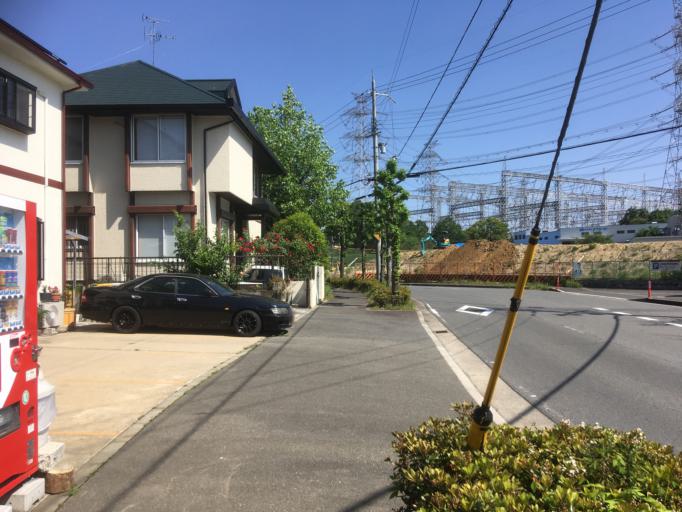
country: JP
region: Nara
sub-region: Ikoma-shi
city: Ikoma
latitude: 34.7390
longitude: 135.7140
